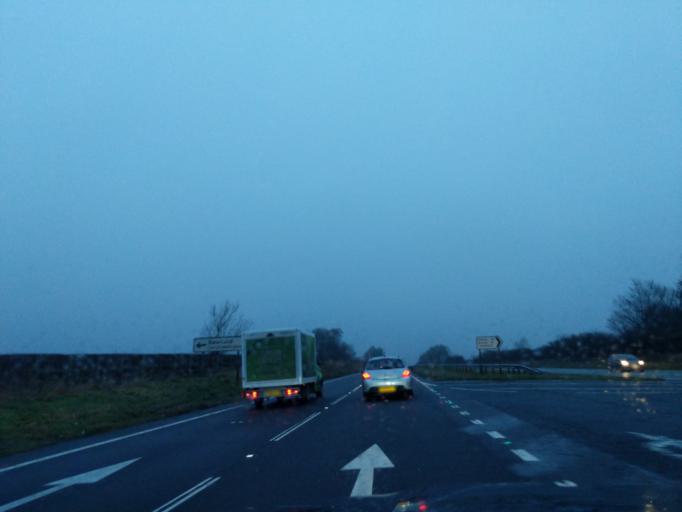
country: GB
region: England
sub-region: Northumberland
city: Felton
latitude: 55.3157
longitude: -1.7252
